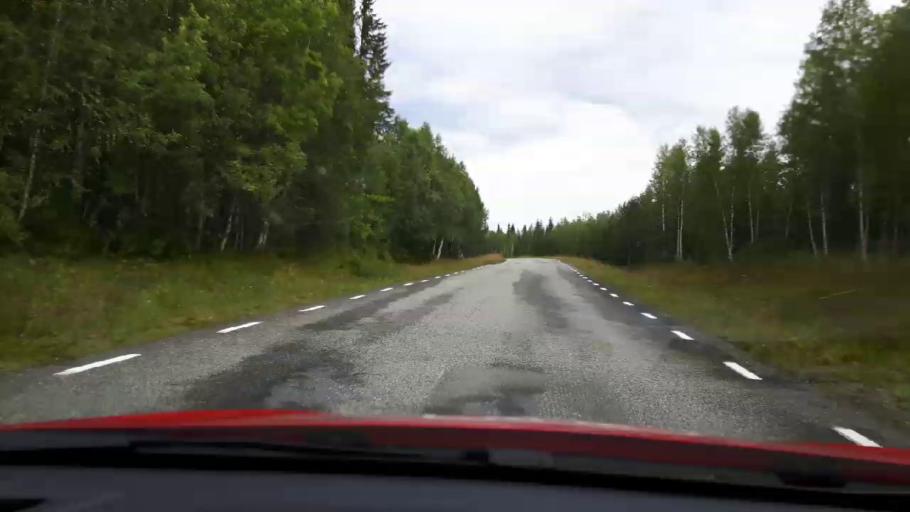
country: SE
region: Jaemtland
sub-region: Are Kommun
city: Are
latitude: 63.7150
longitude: 12.9622
